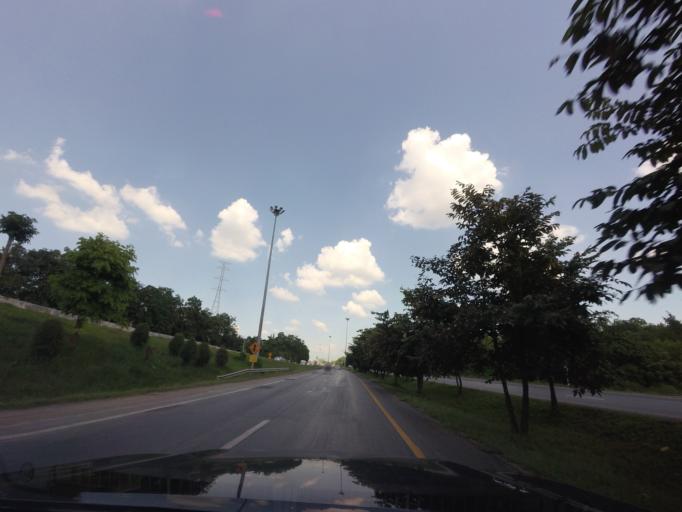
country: TH
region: Nakhon Ratchasima
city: Nakhon Ratchasima
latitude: 15.0564
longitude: 102.1588
